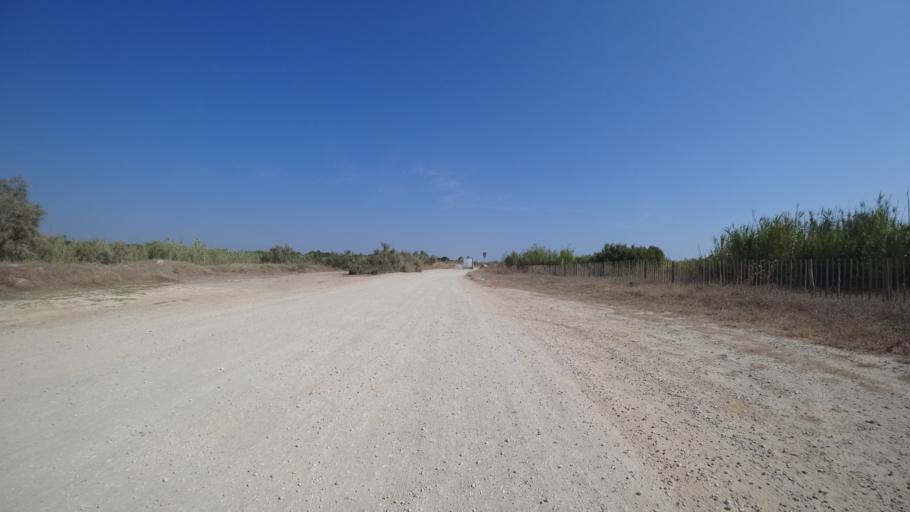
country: FR
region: Languedoc-Roussillon
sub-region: Departement des Pyrenees-Orientales
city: Le Barcares
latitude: 42.7725
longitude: 3.0358
